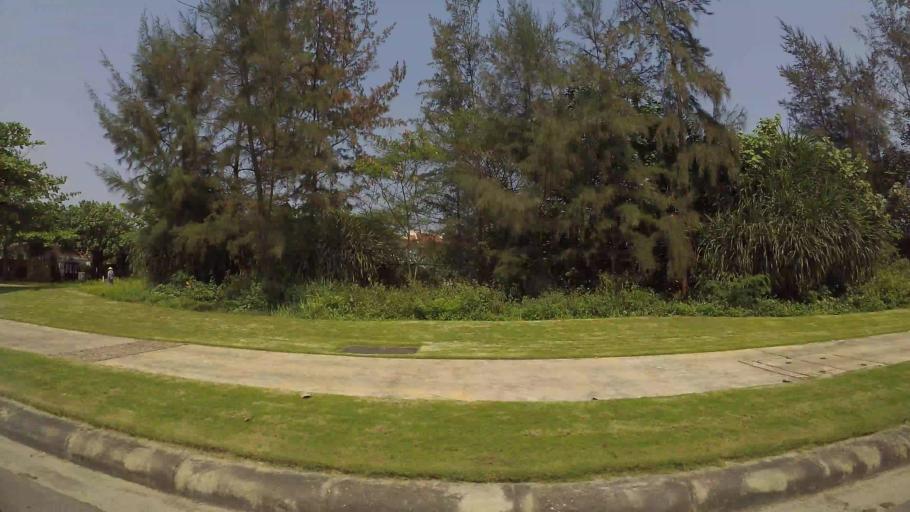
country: VN
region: Da Nang
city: Ngu Hanh Son
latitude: 15.9756
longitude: 108.2790
